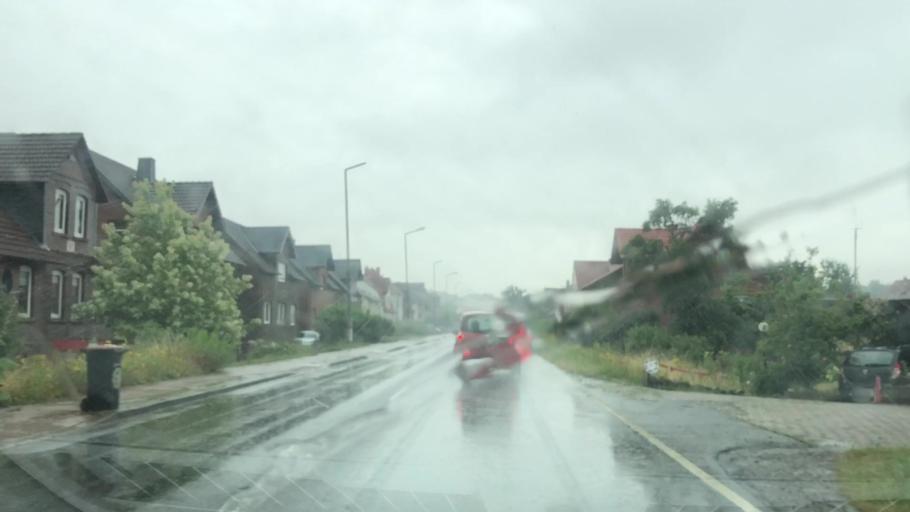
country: DE
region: North Rhine-Westphalia
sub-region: Regierungsbezirk Detmold
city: Minden
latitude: 52.2722
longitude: 8.9714
